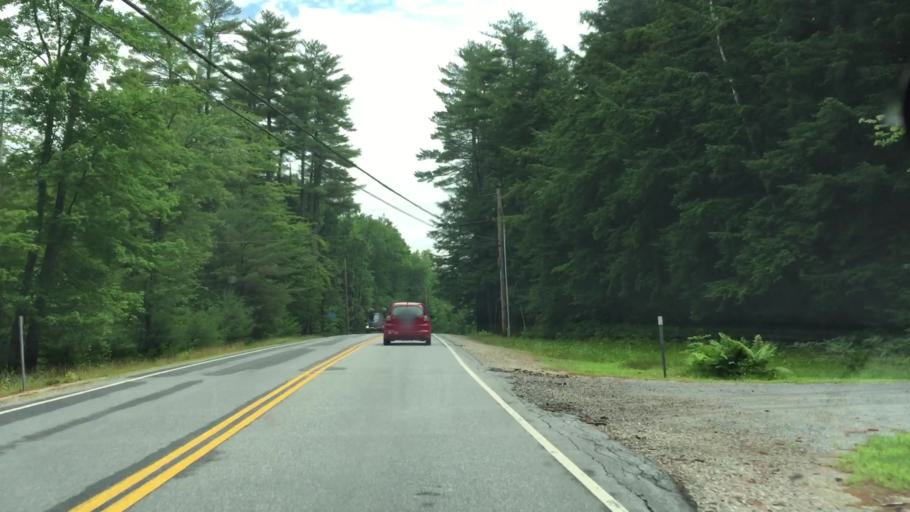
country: US
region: New Hampshire
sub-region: Carroll County
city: Sandwich
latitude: 43.7920
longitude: -71.4548
